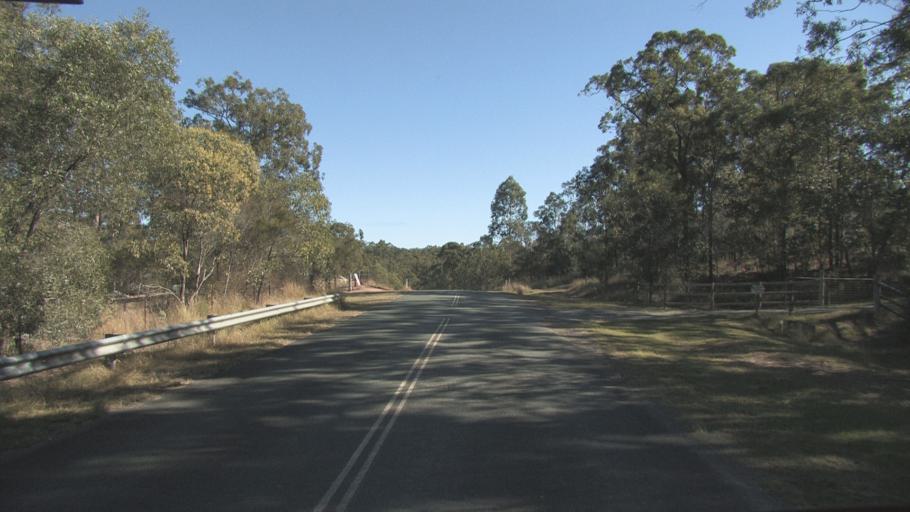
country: AU
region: Queensland
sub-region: Ipswich
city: Springfield Lakes
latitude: -27.7094
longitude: 152.9203
